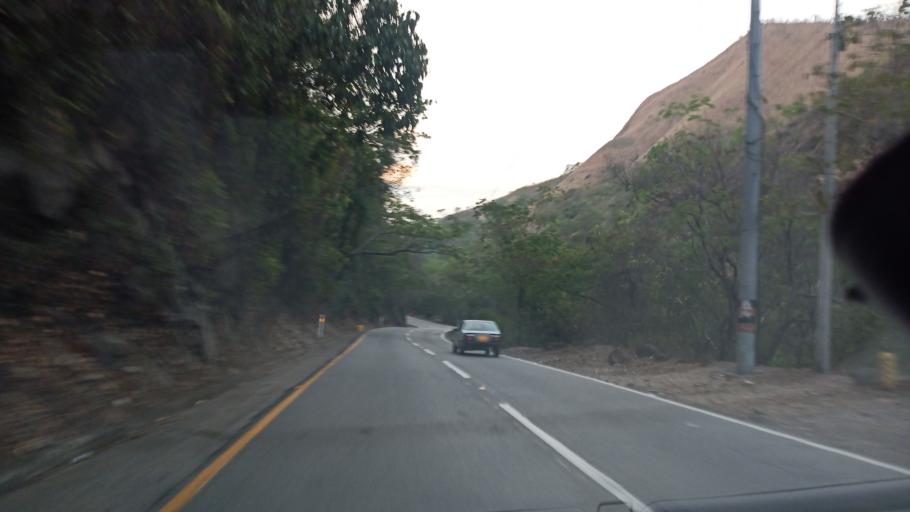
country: CO
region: Cundinamarca
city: Nilo
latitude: 4.2687
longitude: -74.5733
